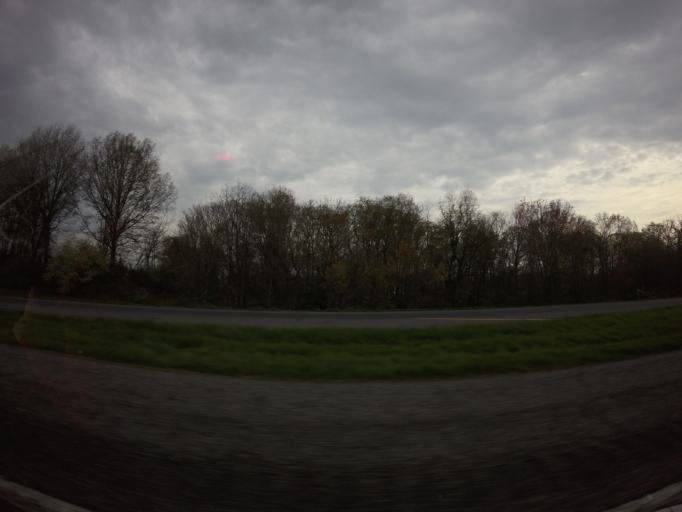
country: US
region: Maryland
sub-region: Howard County
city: Columbia
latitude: 39.3023
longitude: -76.9077
